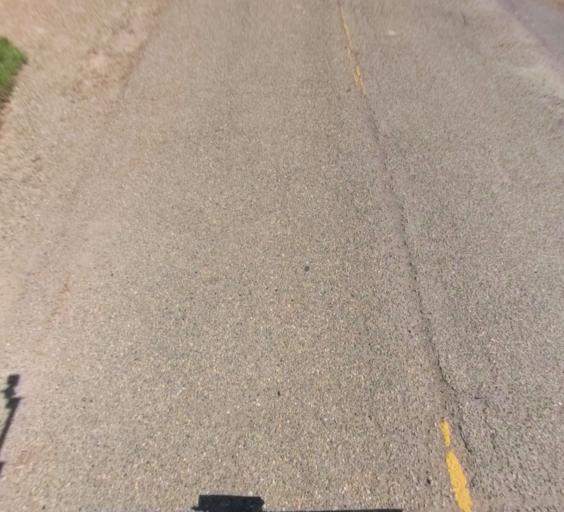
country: US
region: California
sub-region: Madera County
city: Bonadelle Ranchos-Madera Ranchos
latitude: 36.9068
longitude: -119.7956
